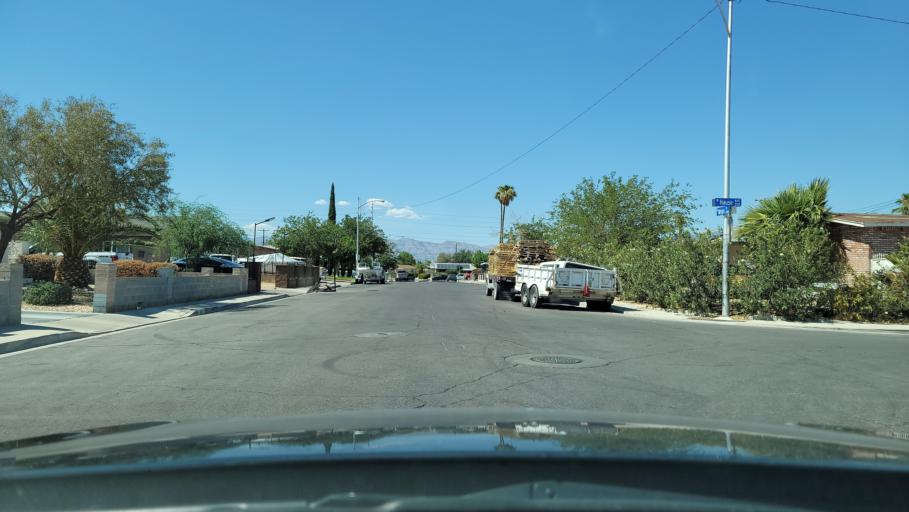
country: US
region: Nevada
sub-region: Clark County
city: Las Vegas
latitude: 36.1999
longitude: -115.1511
